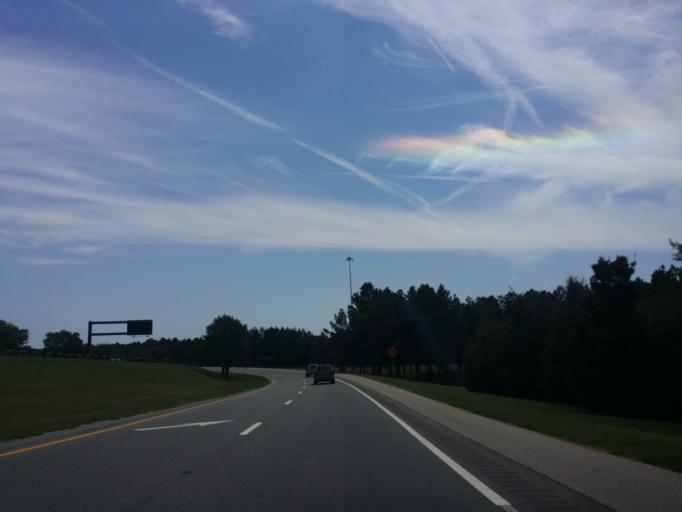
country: US
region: North Carolina
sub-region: Wake County
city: Morrisville
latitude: 35.8643
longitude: -78.8047
